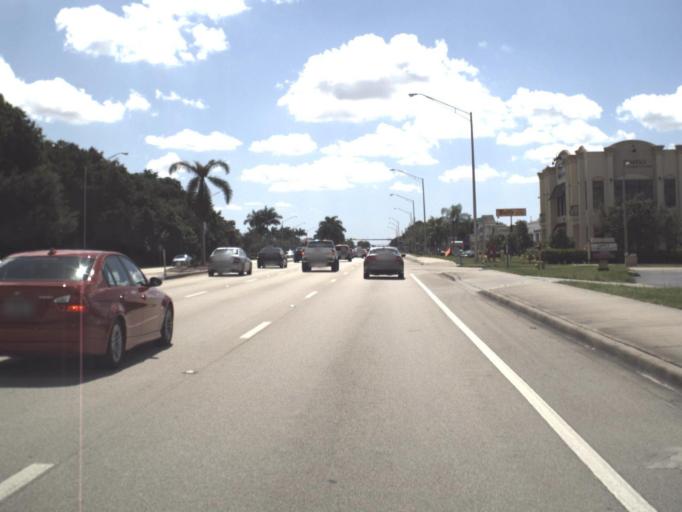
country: US
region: Florida
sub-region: Collier County
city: Naples Park
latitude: 26.2587
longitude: -81.8015
